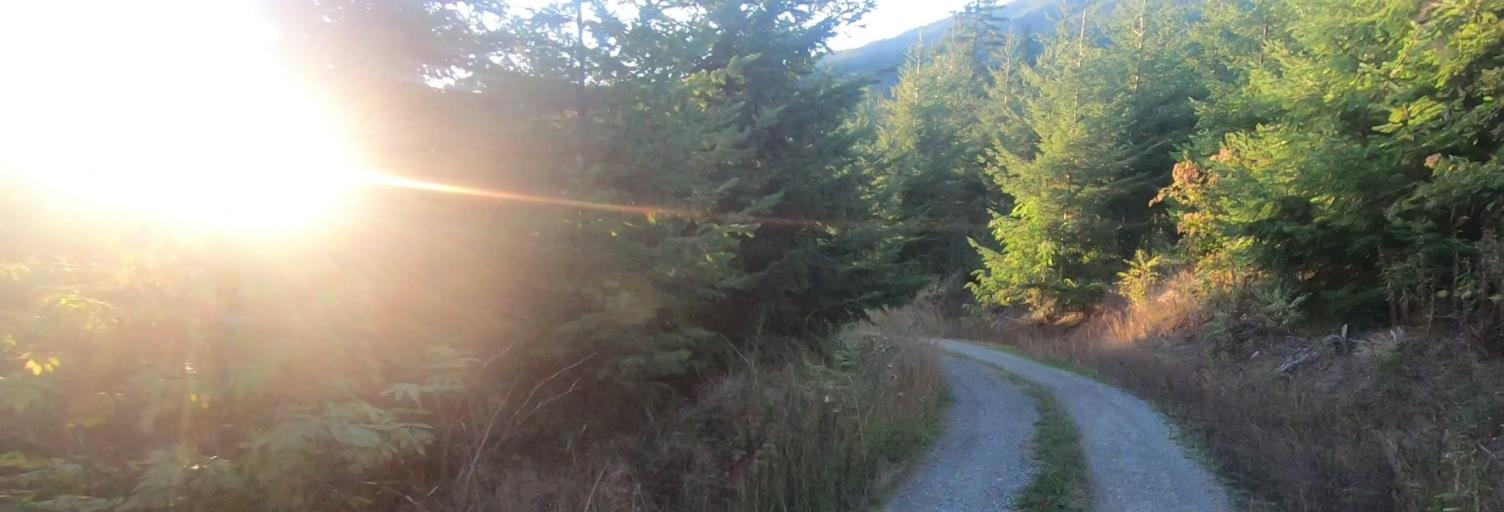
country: US
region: Washington
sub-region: Whatcom County
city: Peaceful Valley
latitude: 48.9220
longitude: -121.9607
